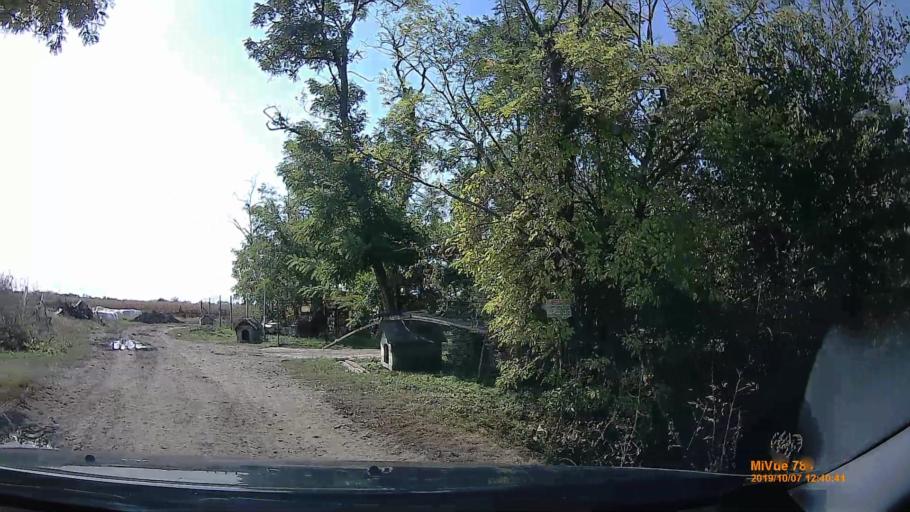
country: HU
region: Jasz-Nagykun-Szolnok
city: Kunszentmarton
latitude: 46.8704
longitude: 20.2612
